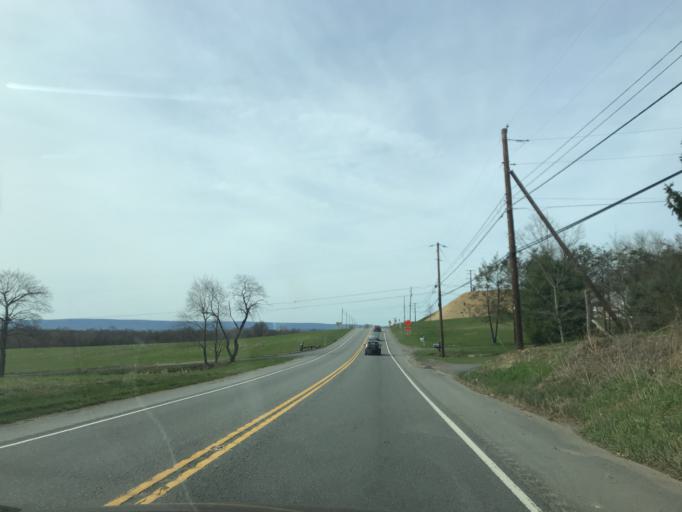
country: US
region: Pennsylvania
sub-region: Union County
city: Lewisburg
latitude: 40.9314
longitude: -76.8484
